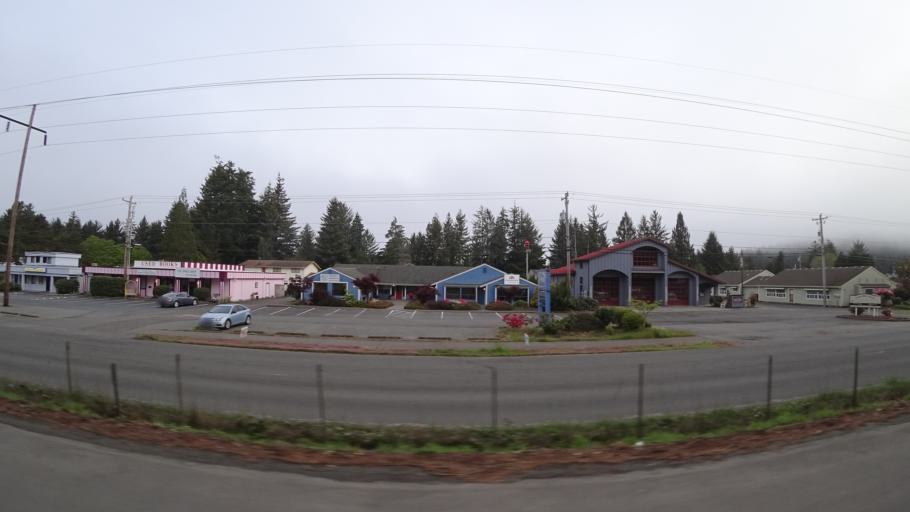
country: US
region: Oregon
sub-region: Douglas County
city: Reedsport
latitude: 43.6941
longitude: -124.1265
